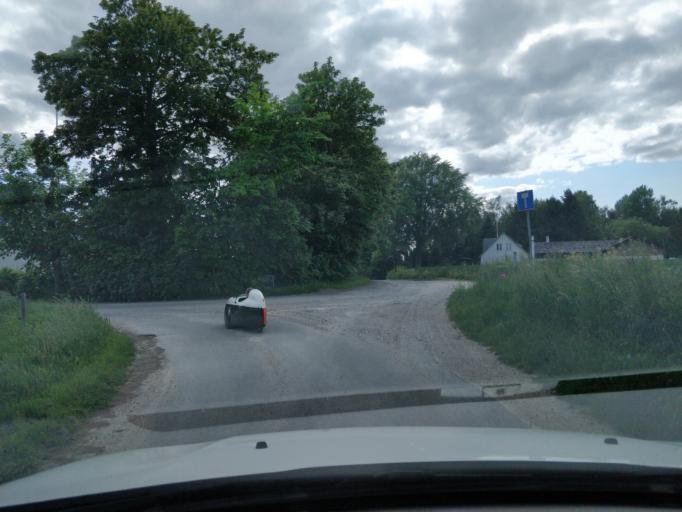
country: DK
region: Capital Region
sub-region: Hoje-Taastrup Kommune
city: Flong
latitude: 55.6890
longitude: 12.2198
